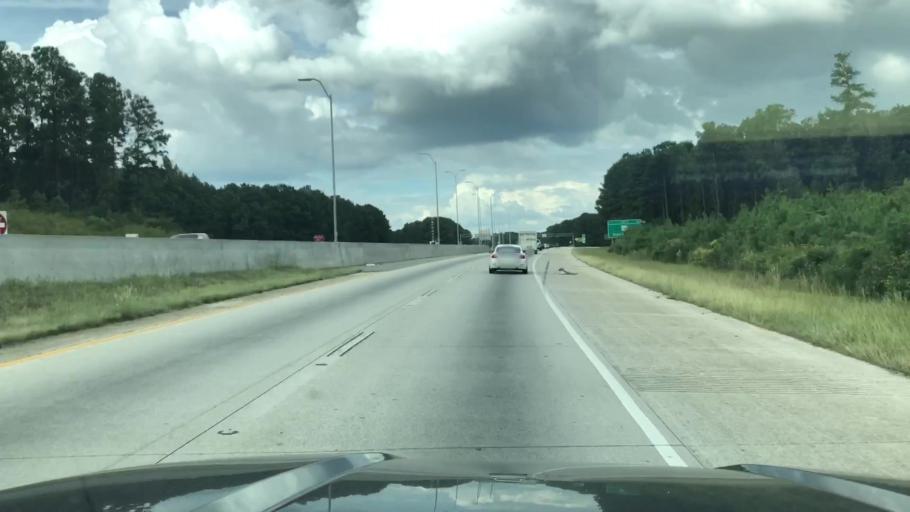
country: US
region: Georgia
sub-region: Henry County
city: Stockbridge
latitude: 33.5476
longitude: -84.2687
